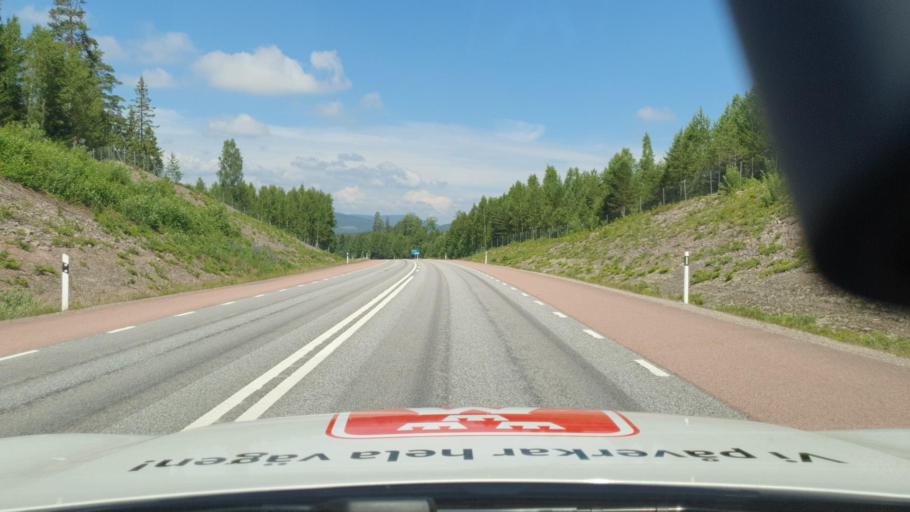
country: SE
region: Vaermland
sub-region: Torsby Kommun
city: Torsby
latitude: 60.1961
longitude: 13.0224
